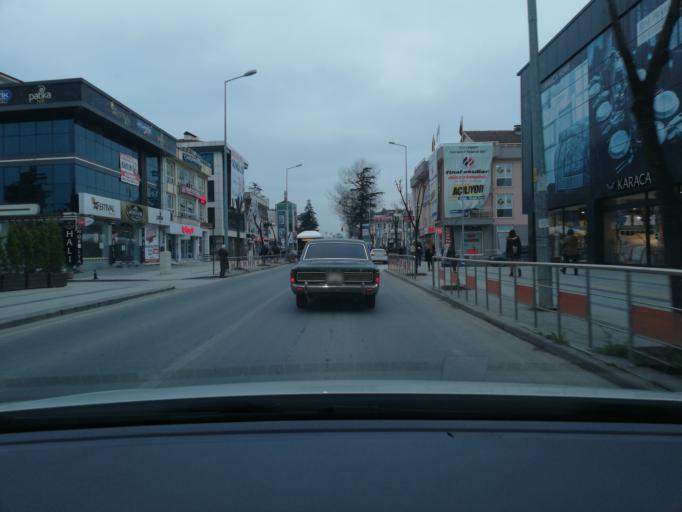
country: TR
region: Duzce
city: Duzce
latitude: 40.8403
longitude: 31.1493
